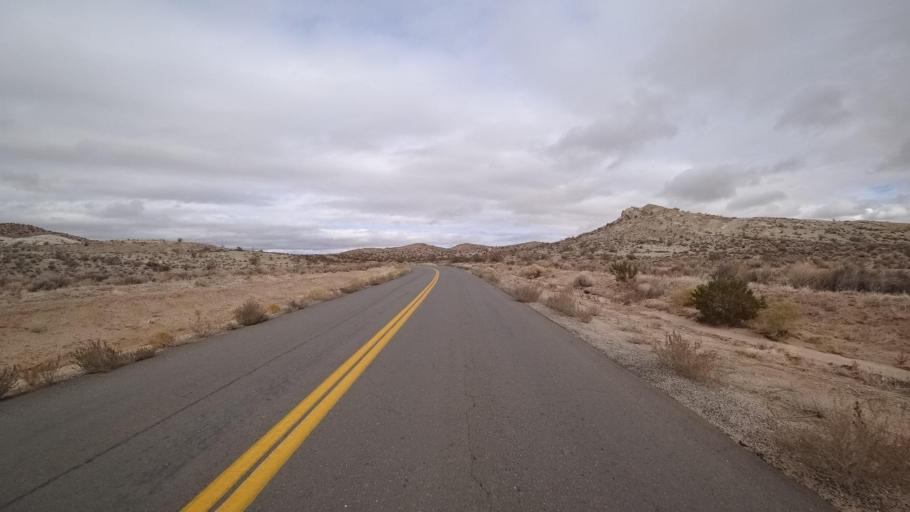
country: US
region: California
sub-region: Kern County
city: Rosamond
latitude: 34.9046
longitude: -118.2149
